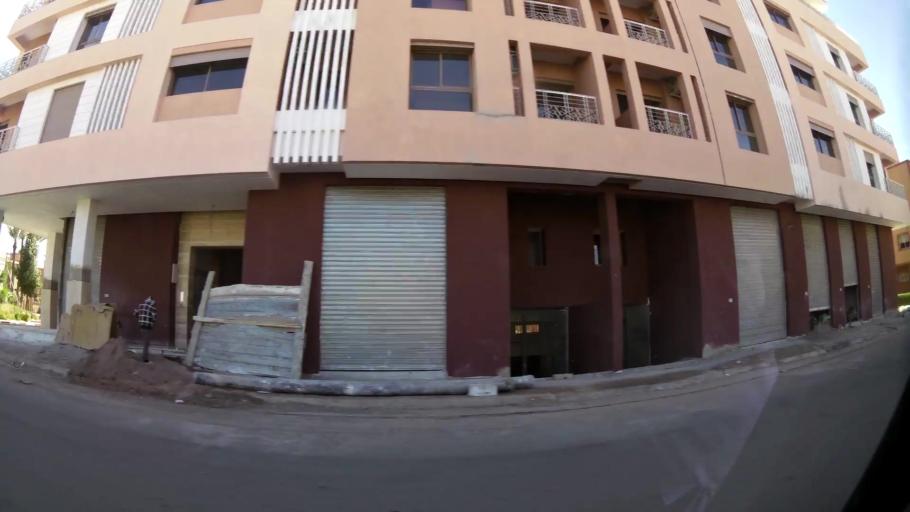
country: MA
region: Marrakech-Tensift-Al Haouz
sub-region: Marrakech
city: Marrakesh
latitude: 31.6654
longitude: -8.0255
